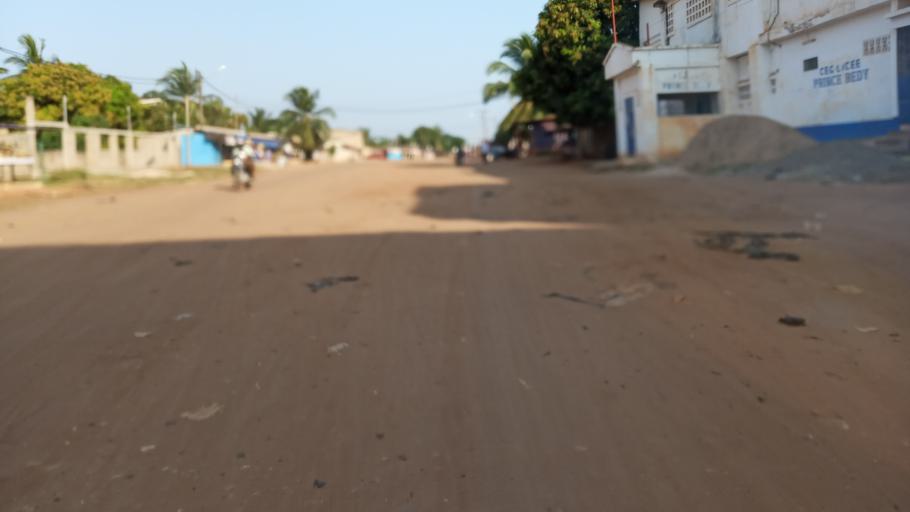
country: TG
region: Maritime
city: Lome
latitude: 6.1813
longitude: 1.1562
